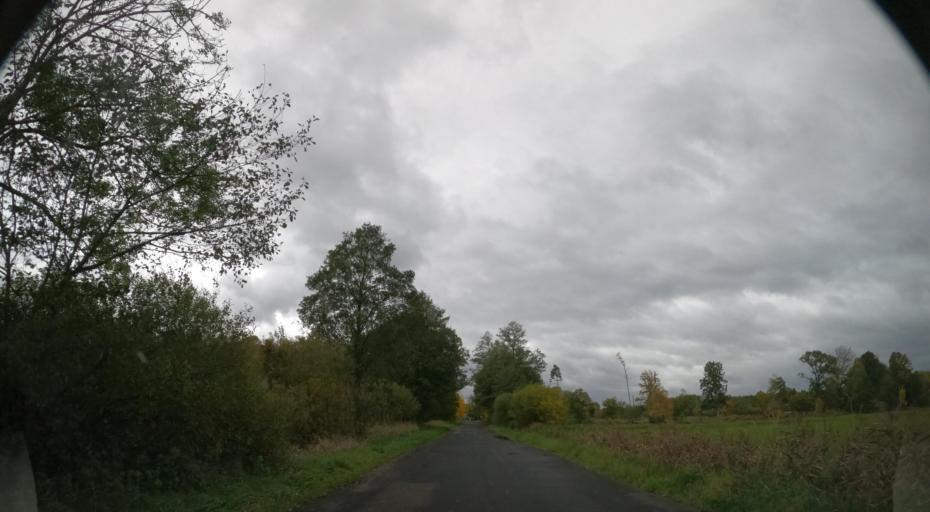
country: PL
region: West Pomeranian Voivodeship
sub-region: Powiat goleniowski
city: Stepnica
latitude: 53.6593
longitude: 14.6611
